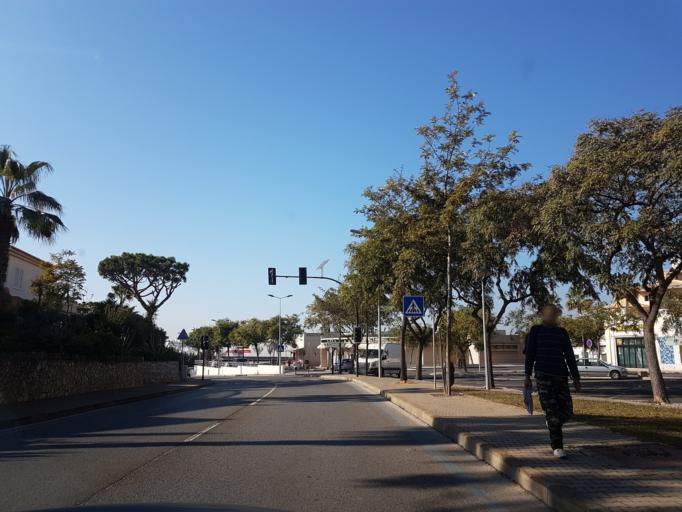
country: PT
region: Faro
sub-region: Loule
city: Boliqueime
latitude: 37.0936
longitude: -8.1929
